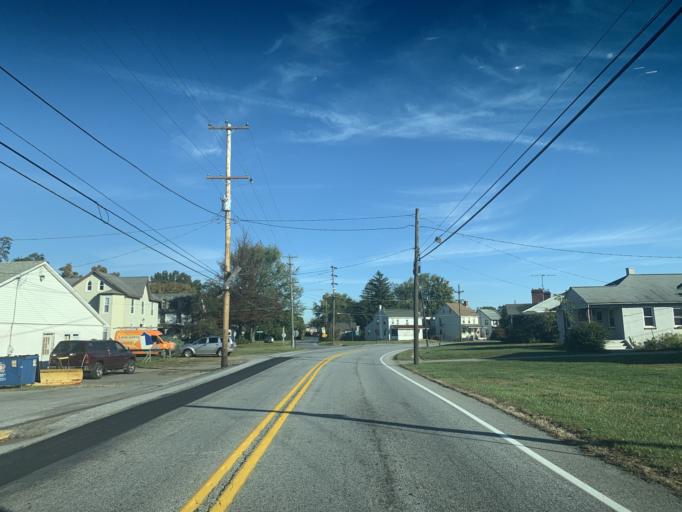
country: US
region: Pennsylvania
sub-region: Chester County
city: Parkesburg
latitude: 39.8899
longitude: -75.9230
